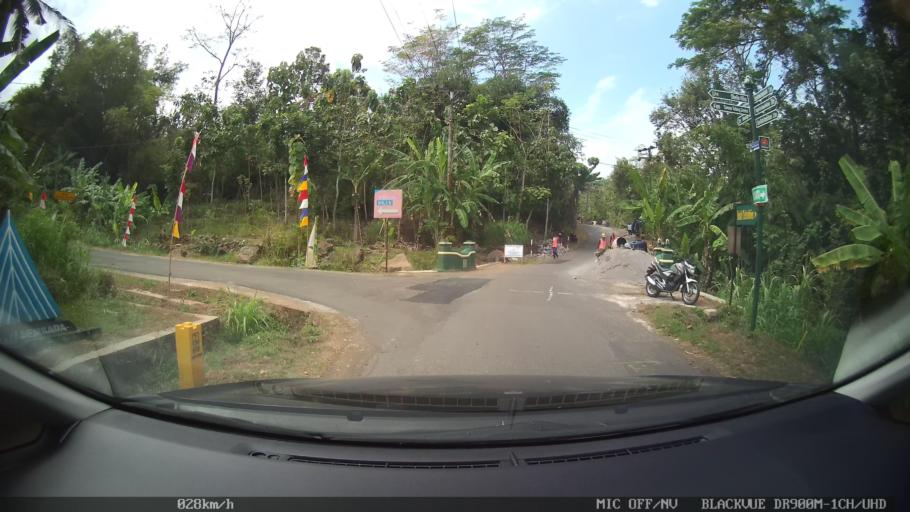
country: ID
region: Central Java
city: Candi Prambanan
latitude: -7.8202
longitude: 110.5235
